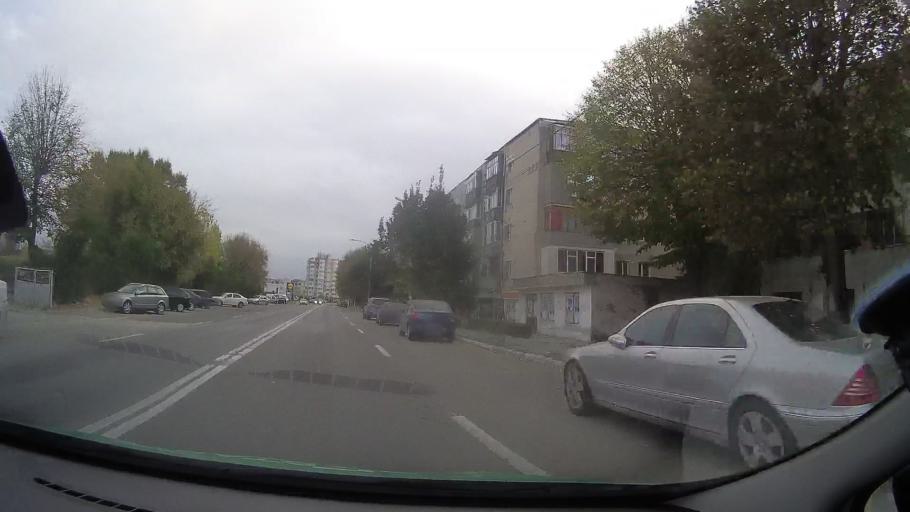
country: RO
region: Constanta
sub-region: Municipiul Medgidia
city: Medgidia
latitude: 44.2637
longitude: 28.2604
